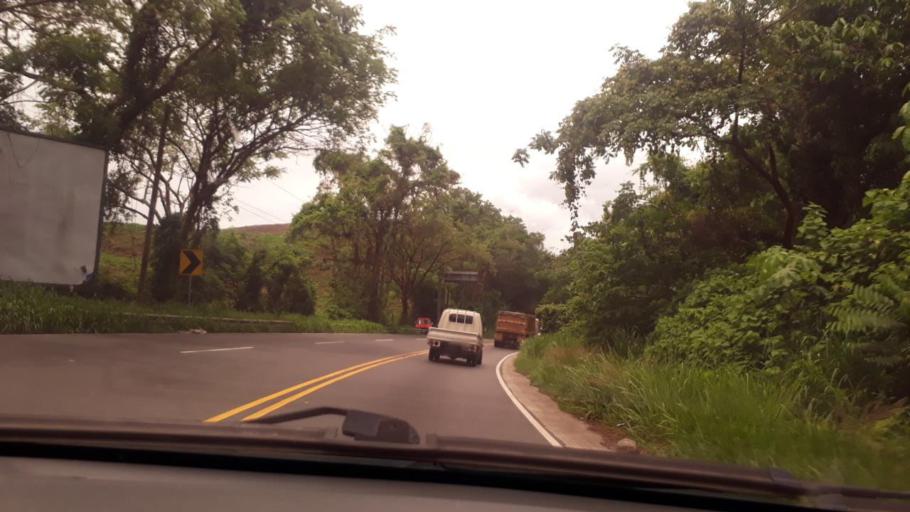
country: GT
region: Izabal
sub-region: Municipio de Los Amates
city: Los Amates
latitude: 15.2453
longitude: -89.1356
